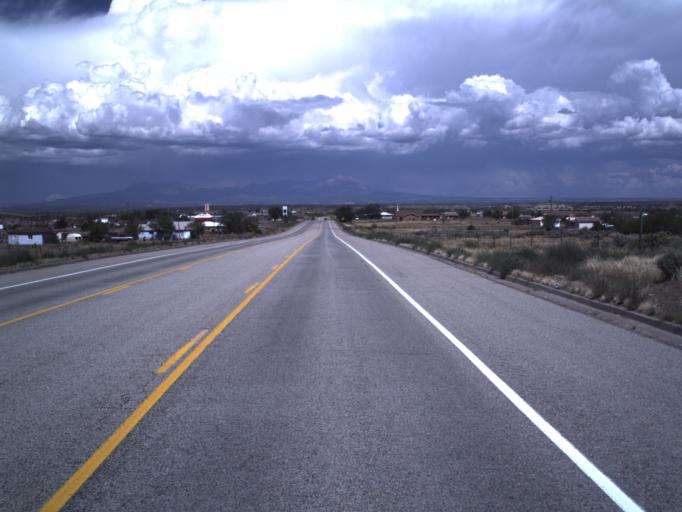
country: US
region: Utah
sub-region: San Juan County
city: Blanding
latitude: 37.4606
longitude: -109.4670
